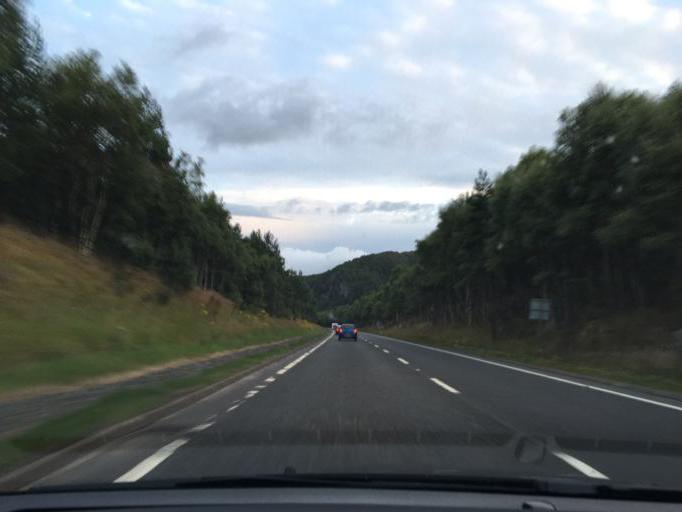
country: GB
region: Scotland
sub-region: Highland
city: Aviemore
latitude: 57.1960
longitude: -3.8360
